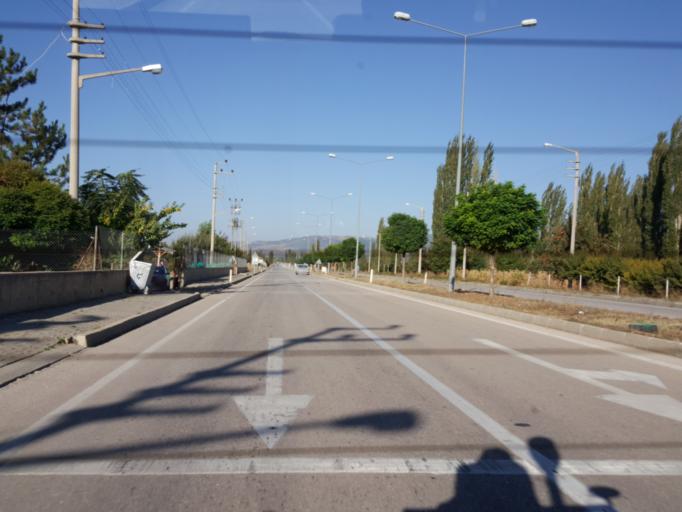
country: TR
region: Amasya
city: Ezinepazari
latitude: 40.5707
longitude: 36.1336
